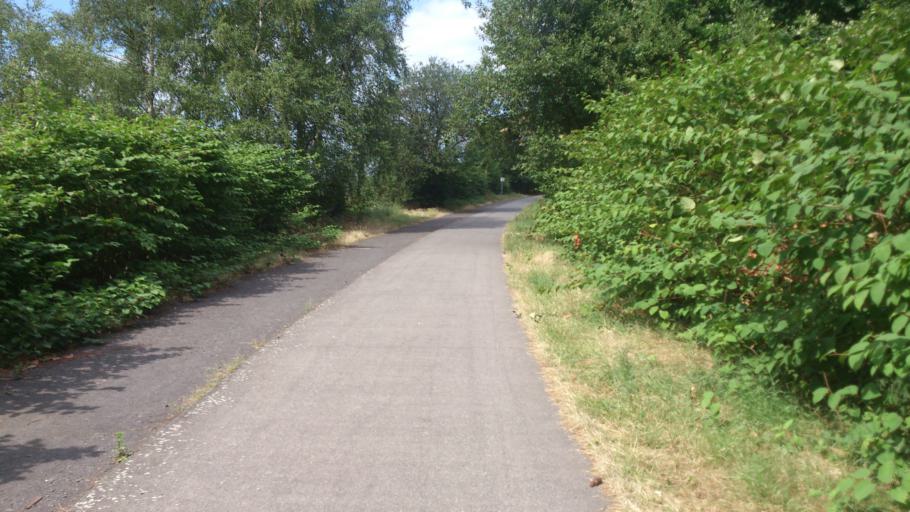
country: BE
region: Wallonia
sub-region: Province de Liege
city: Herstal
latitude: 50.6328
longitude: 5.6234
